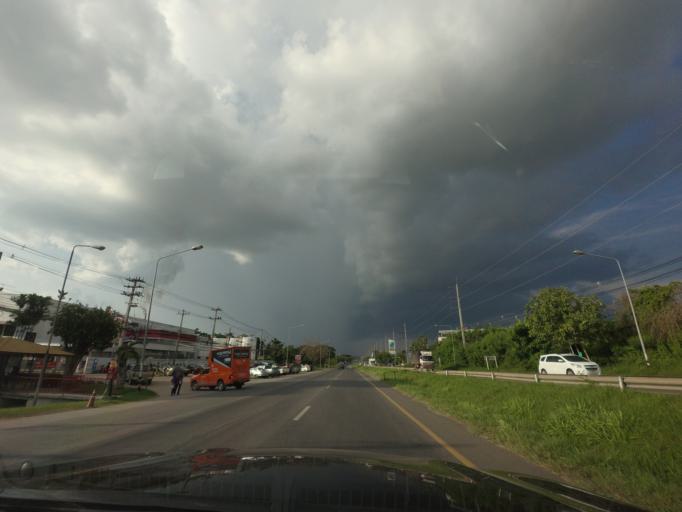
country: TH
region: Khon Kaen
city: Khon Kaen
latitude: 16.3485
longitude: 102.8032
